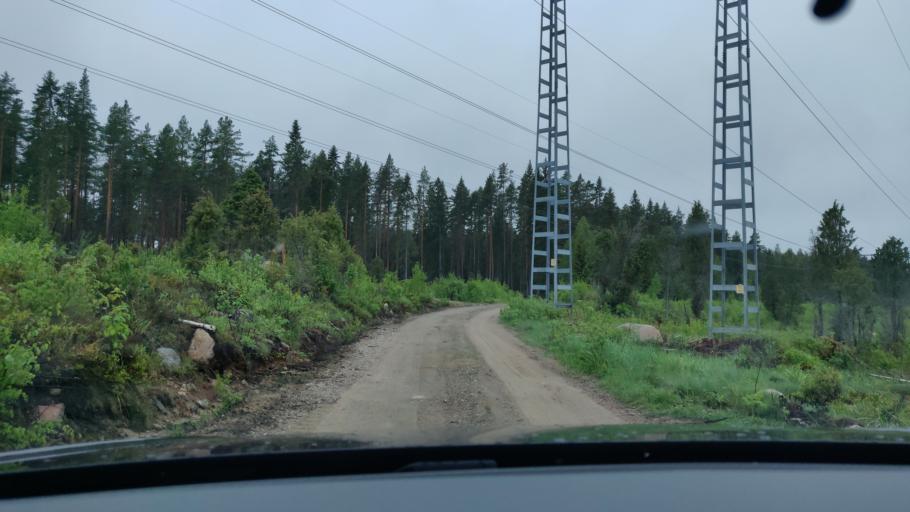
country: SE
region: Dalarna
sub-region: Avesta Kommun
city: Horndal
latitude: 60.3169
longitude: 16.3981
